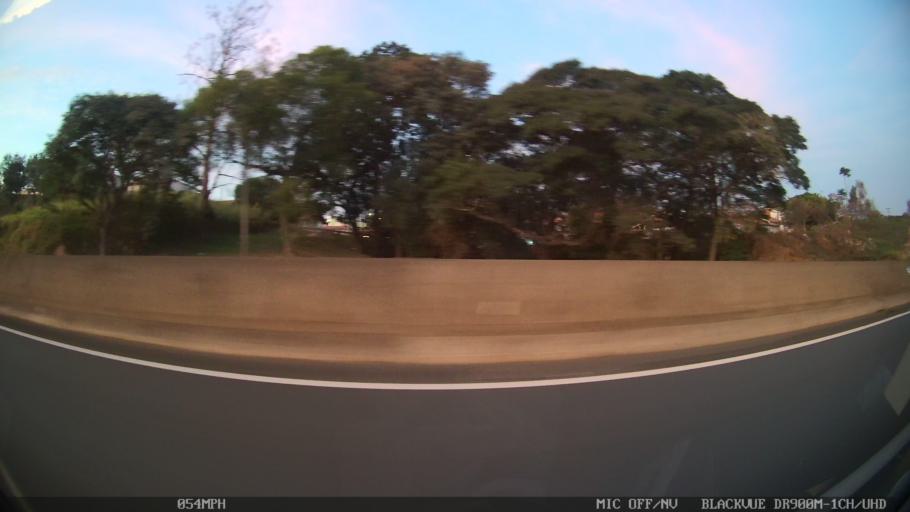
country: BR
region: Sao Paulo
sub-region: Vinhedo
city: Vinhedo
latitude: -23.0389
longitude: -47.0087
